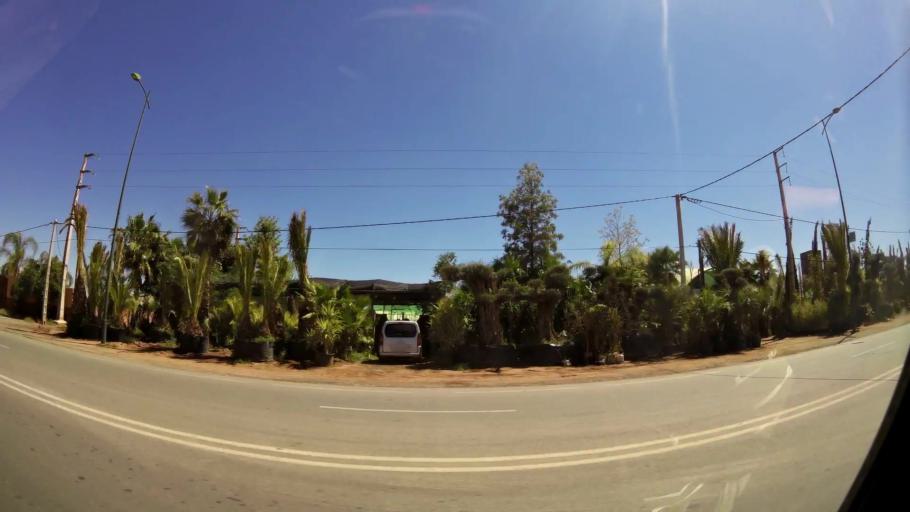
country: MA
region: Marrakech-Tensift-Al Haouz
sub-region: Marrakech
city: Marrakesh
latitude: 31.5601
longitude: -7.9779
